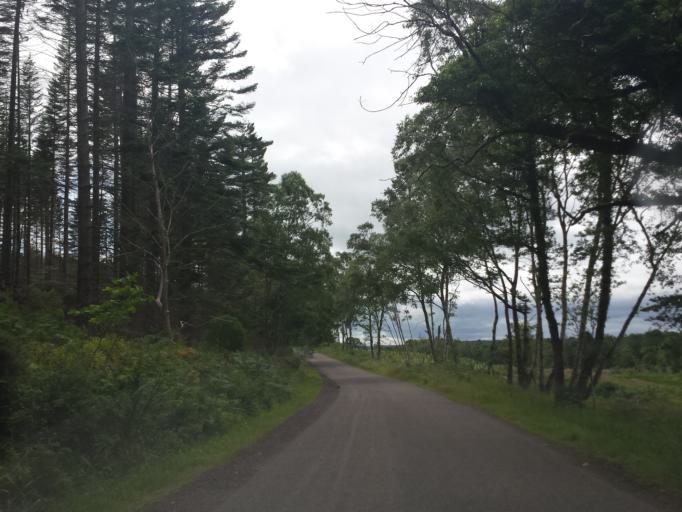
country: GB
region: Scotland
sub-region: Highland
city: Nairn
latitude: 57.5151
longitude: -3.9718
